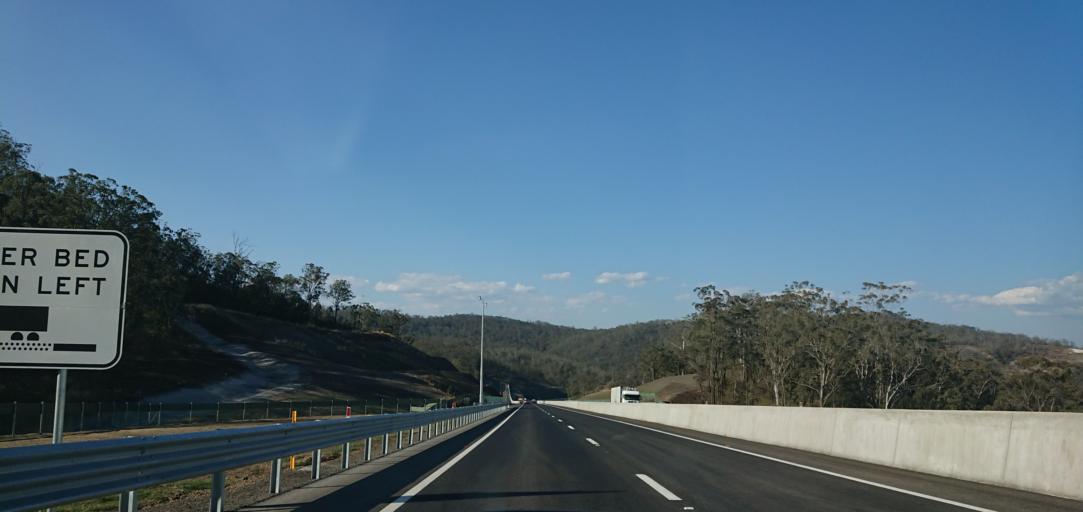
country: AU
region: Queensland
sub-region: Toowoomba
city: Wilsonton Heights
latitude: -27.5061
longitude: 151.9711
